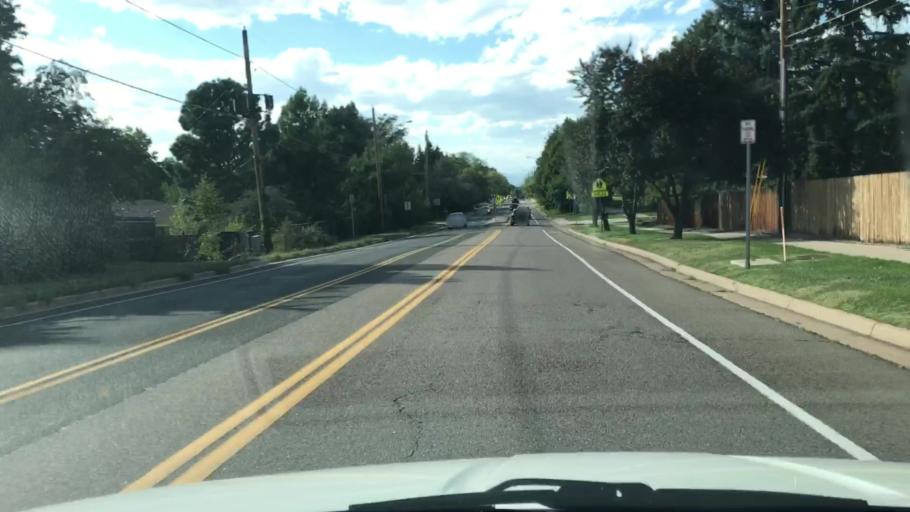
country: US
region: Colorado
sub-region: Arapahoe County
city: Cherry Hills Village
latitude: 39.6439
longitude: -104.9199
